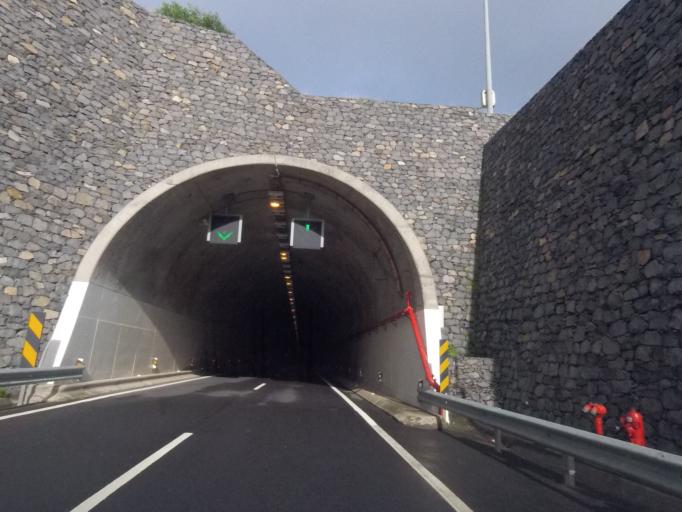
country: PT
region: Madeira
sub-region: Machico
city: Canical
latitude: 32.7382
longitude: -16.7514
